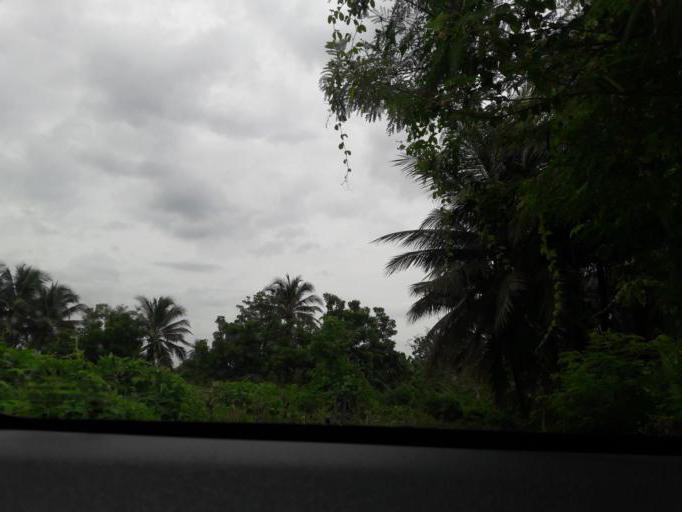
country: TH
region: Ratchaburi
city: Damnoen Saduak
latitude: 13.5718
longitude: 99.9875
